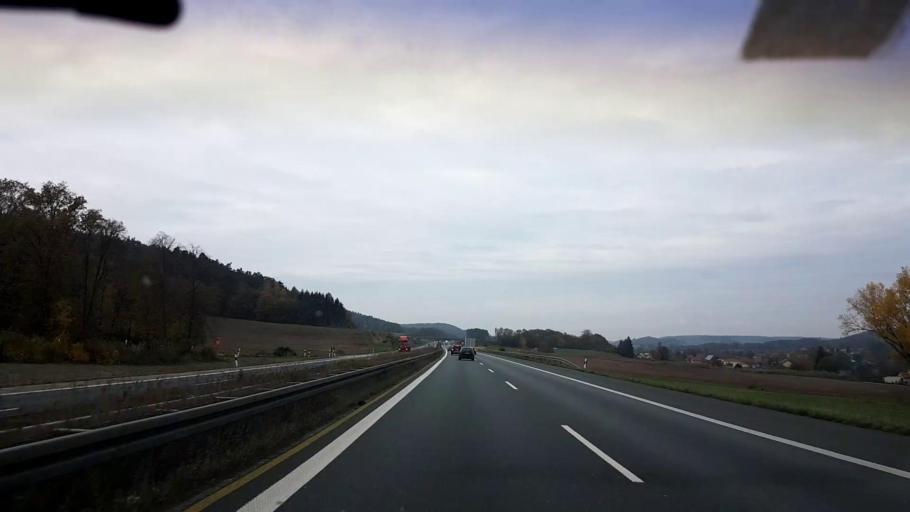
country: DE
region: Bavaria
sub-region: Regierungsbezirk Mittelfranken
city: Markt Taschendorf
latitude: 49.7638
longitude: 10.5417
